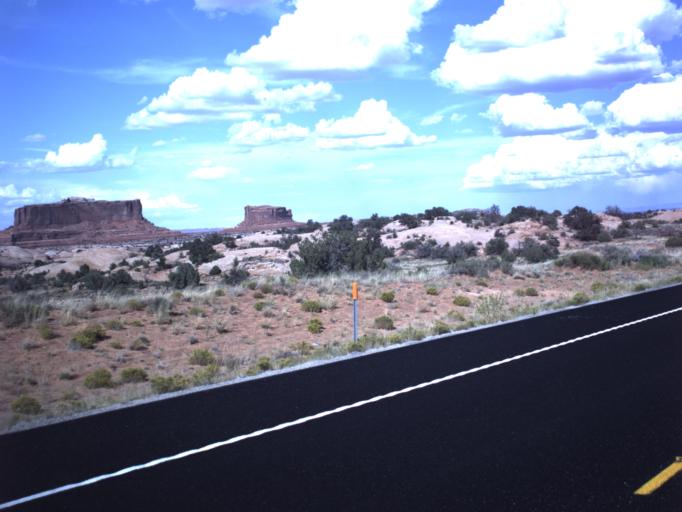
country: US
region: Utah
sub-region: Grand County
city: Moab
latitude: 38.6365
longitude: -109.7638
